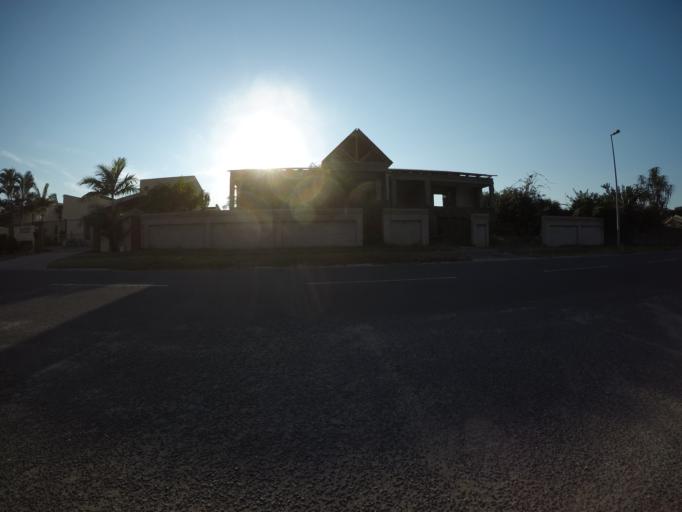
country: ZA
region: KwaZulu-Natal
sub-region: uThungulu District Municipality
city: Richards Bay
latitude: -28.7816
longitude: 32.1118
